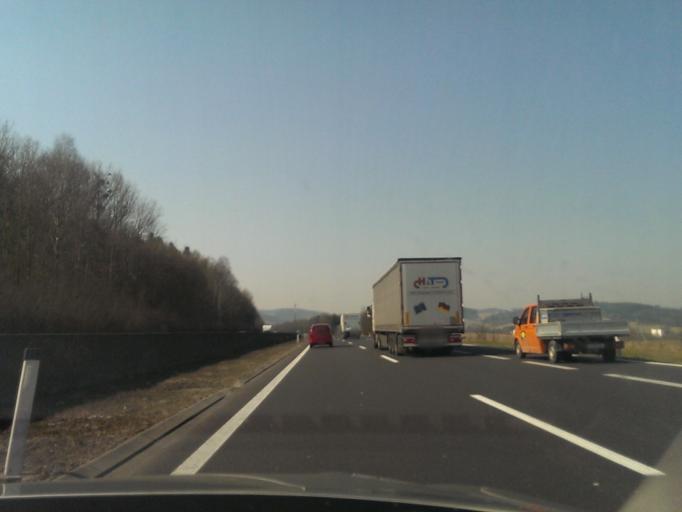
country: AT
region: Upper Austria
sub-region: Politischer Bezirk Grieskirchen
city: Bad Schallerbach
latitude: 48.1886
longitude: 13.9371
